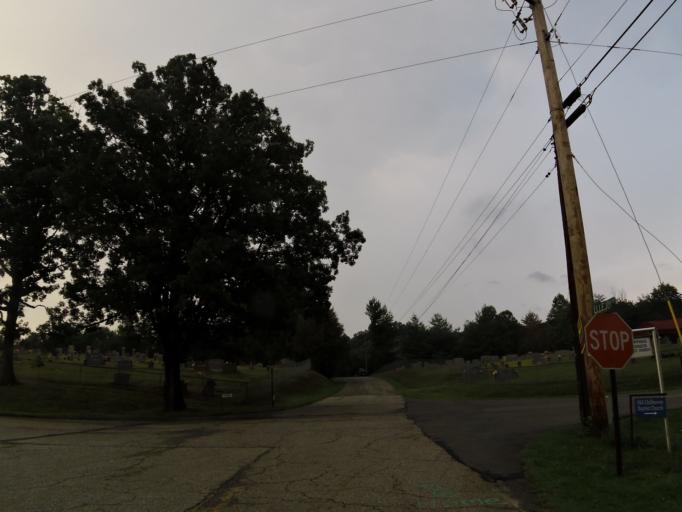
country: US
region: Tennessee
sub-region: Sevier County
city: Seymour
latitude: 35.8096
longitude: -83.7550
